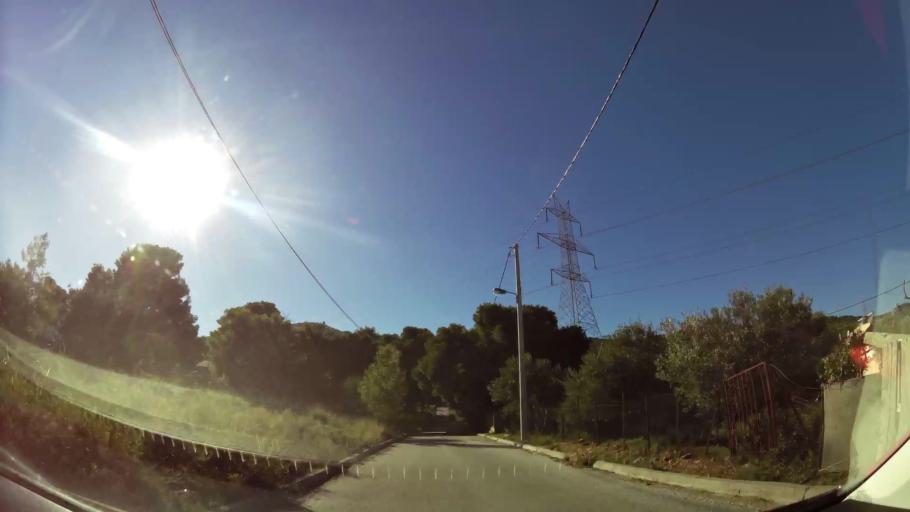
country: GR
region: Attica
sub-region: Nomarchia Anatolikis Attikis
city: Leondarion
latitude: 37.9874
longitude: 23.8432
